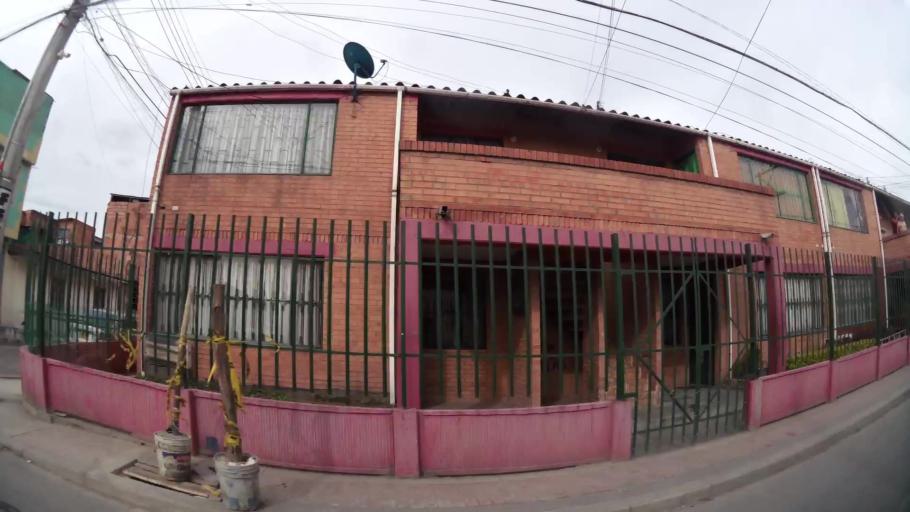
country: CO
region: Cundinamarca
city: Funza
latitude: 4.7066
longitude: -74.2114
